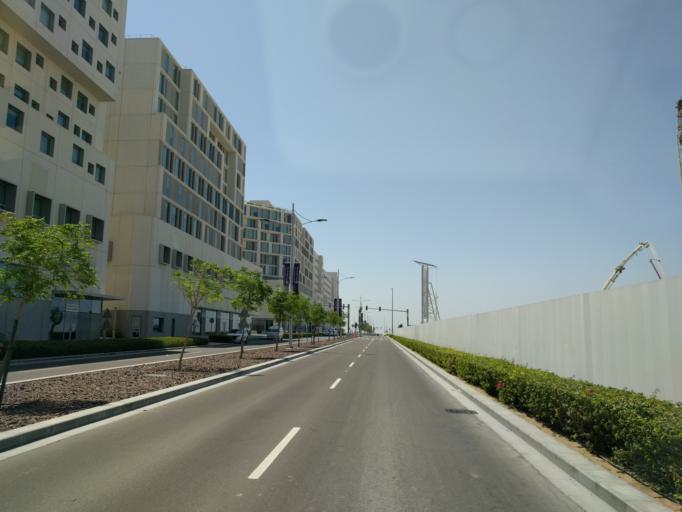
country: AE
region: Abu Dhabi
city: Abu Dhabi
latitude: 24.5242
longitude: 54.4325
